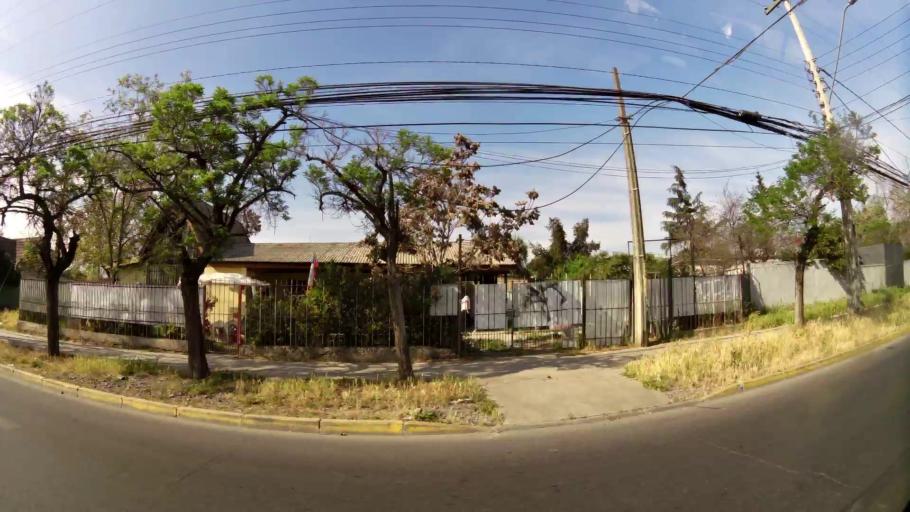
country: CL
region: Santiago Metropolitan
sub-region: Provincia de Cordillera
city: Puente Alto
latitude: -33.5630
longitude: -70.5804
